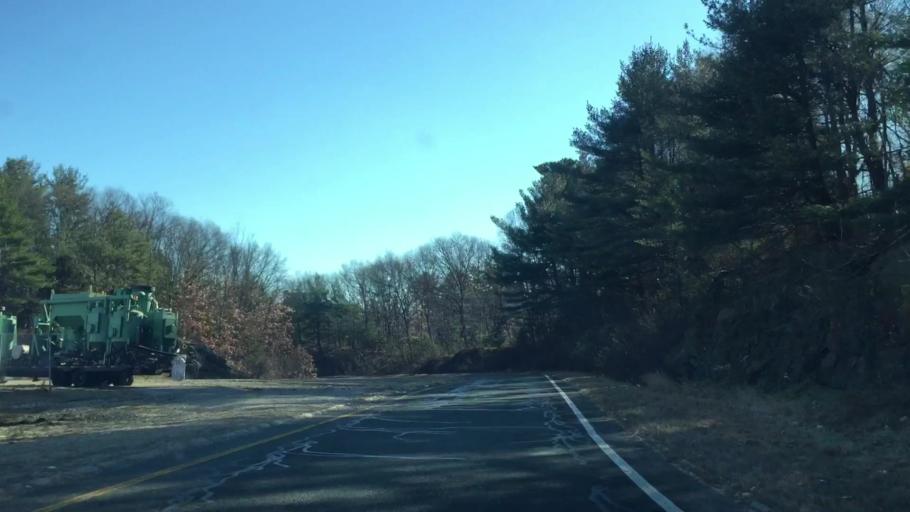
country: US
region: Massachusetts
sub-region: Middlesex County
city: Stoneham
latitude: 42.5022
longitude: -71.1058
